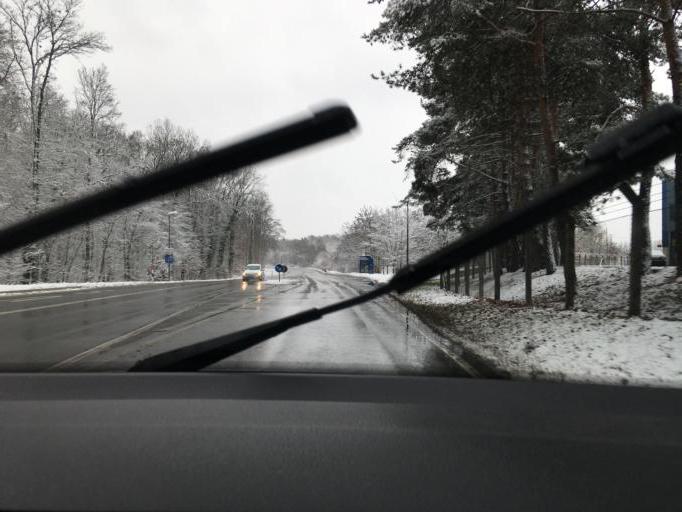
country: DE
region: Baden-Wuerttemberg
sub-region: Freiburg Region
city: Singen
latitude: 47.7626
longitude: 8.8701
